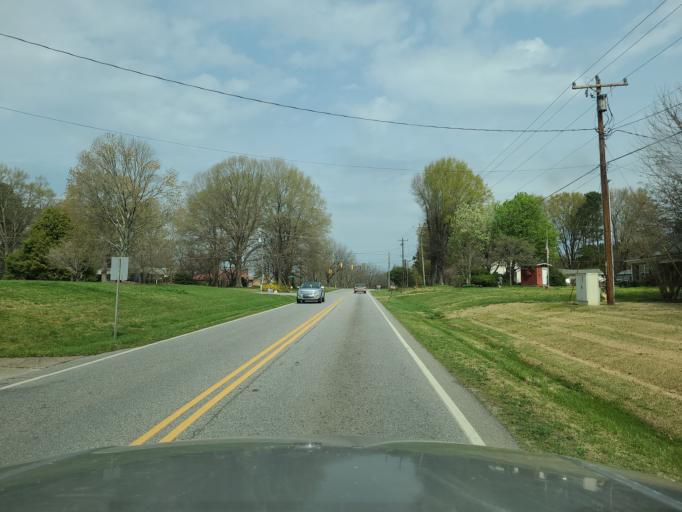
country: US
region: North Carolina
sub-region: Gaston County
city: Stanley
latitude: 35.3357
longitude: -81.0913
